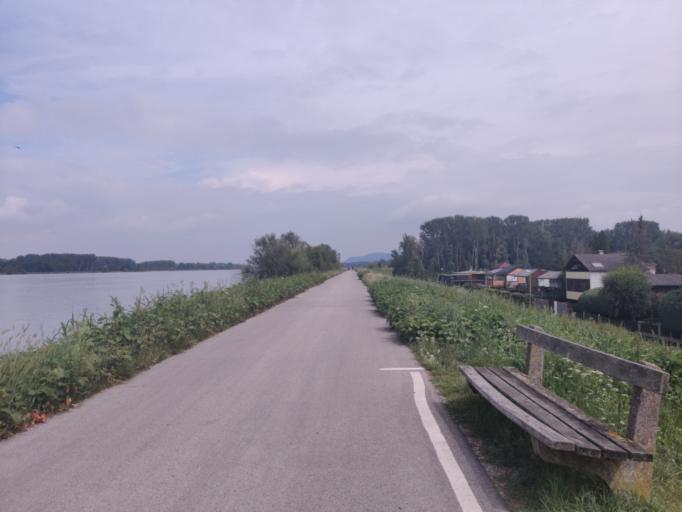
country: AT
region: Lower Austria
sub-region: Politischer Bezirk Tulln
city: Konigstetten
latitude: 48.3363
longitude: 16.1471
